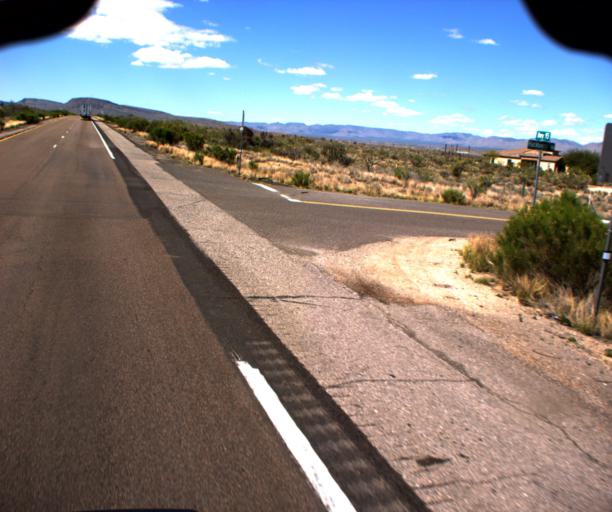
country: US
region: Arizona
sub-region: Mohave County
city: Kingman
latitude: 35.1028
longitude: -113.6658
